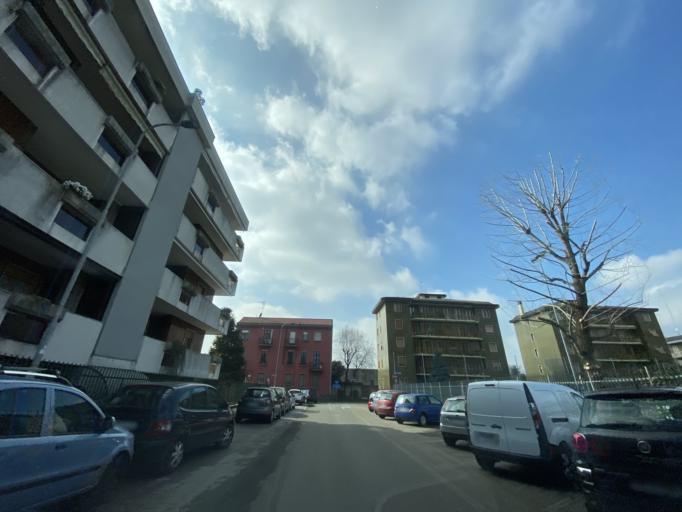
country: IT
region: Lombardy
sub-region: Citta metropolitana di Milano
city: Bresso
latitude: 45.5380
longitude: 9.1856
